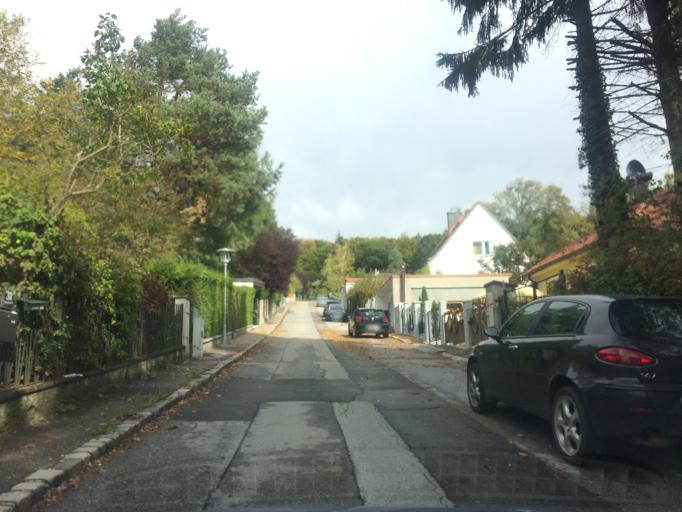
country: AT
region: Lower Austria
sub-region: Politischer Bezirk Wien-Umgebung
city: Gablitz
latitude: 48.2349
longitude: 16.1484
